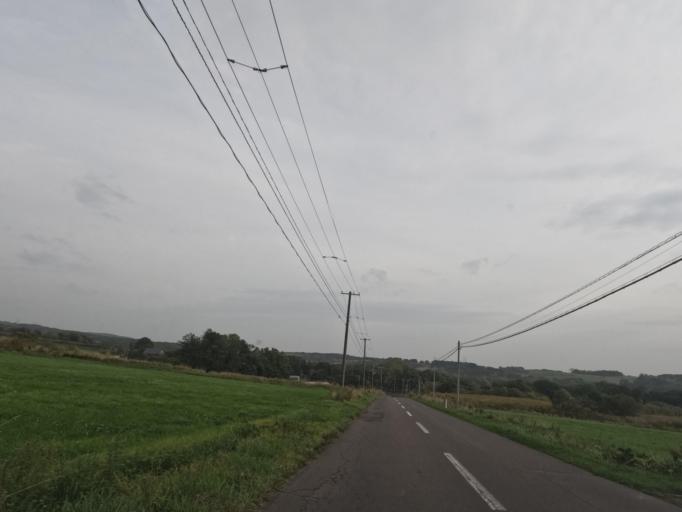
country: JP
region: Hokkaido
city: Date
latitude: 42.4201
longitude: 140.9121
